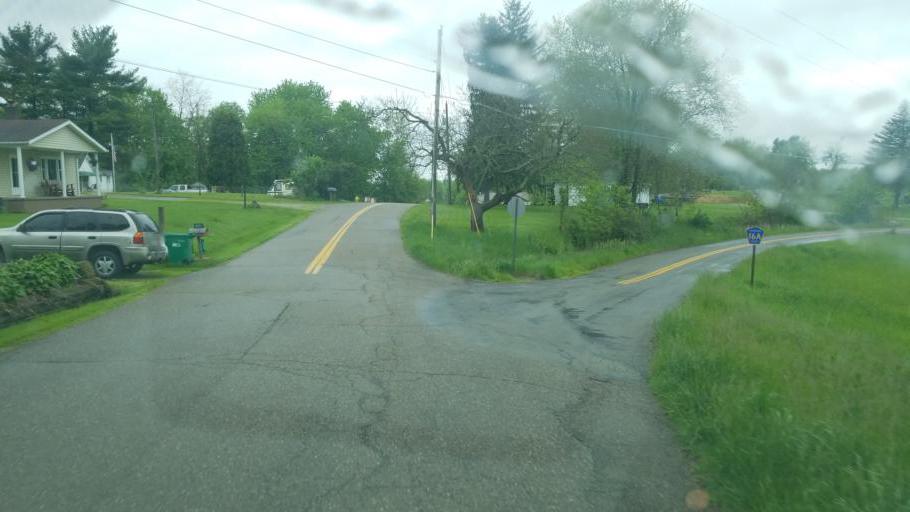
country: US
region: Ohio
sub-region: Jefferson County
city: Tiltonsville
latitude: 40.2221
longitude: -80.7103
